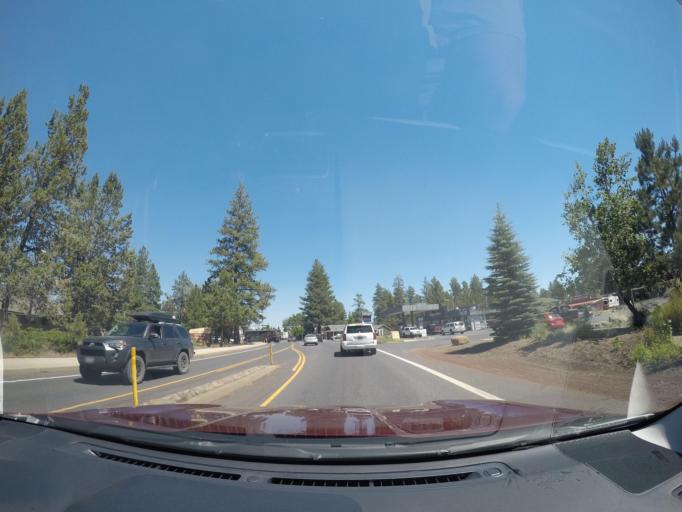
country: US
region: Oregon
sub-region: Deschutes County
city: Sisters
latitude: 44.2914
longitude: -121.5549
